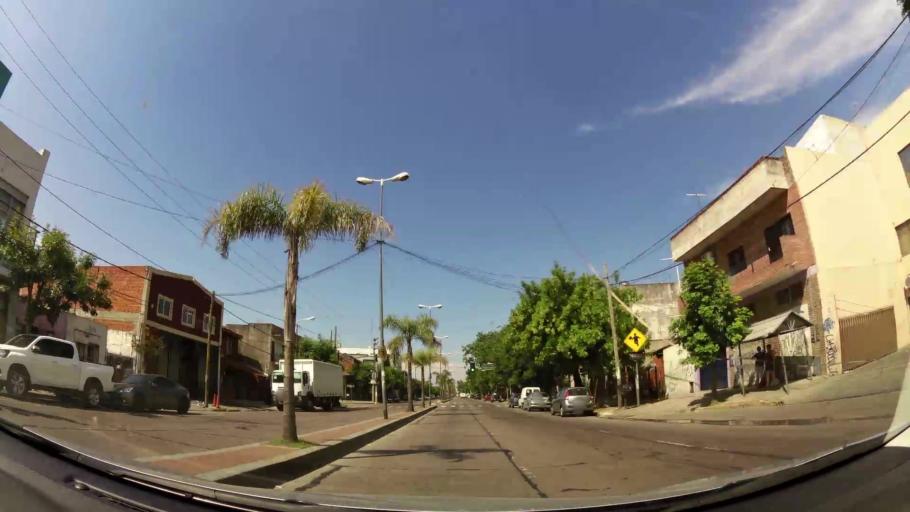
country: AR
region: Buenos Aires
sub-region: Partido de Tigre
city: Tigre
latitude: -34.4687
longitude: -58.5894
